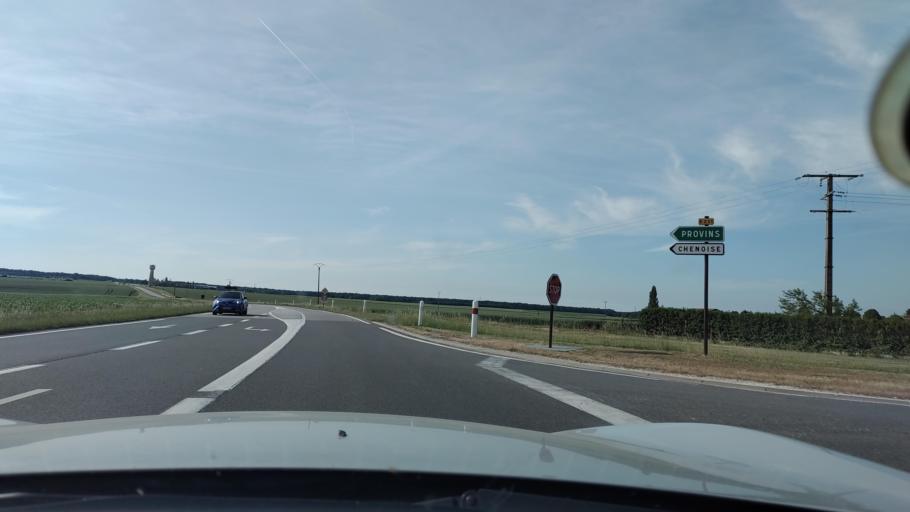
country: FR
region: Ile-de-France
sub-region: Departement de Seine-et-Marne
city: Jouy-le-Chatel
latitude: 48.6619
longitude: 3.1397
